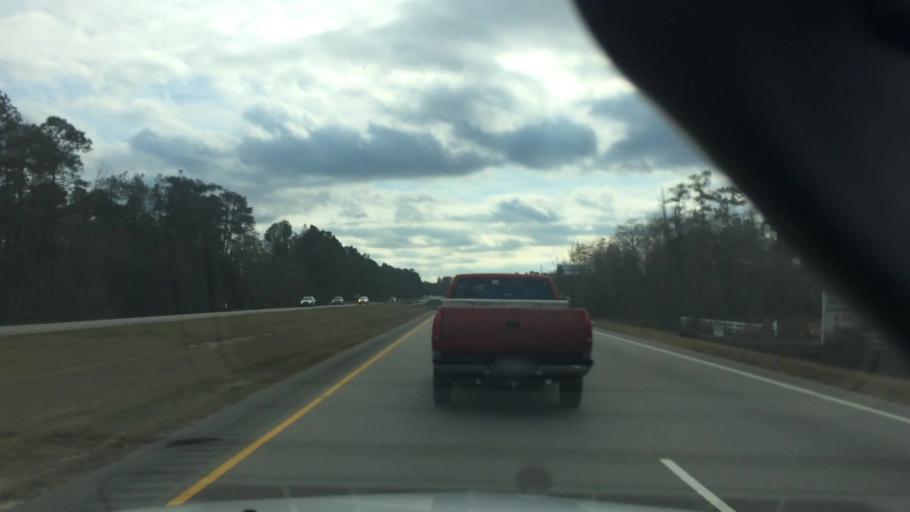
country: US
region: North Carolina
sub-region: Brunswick County
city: Bolivia
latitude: 34.1586
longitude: -78.0916
